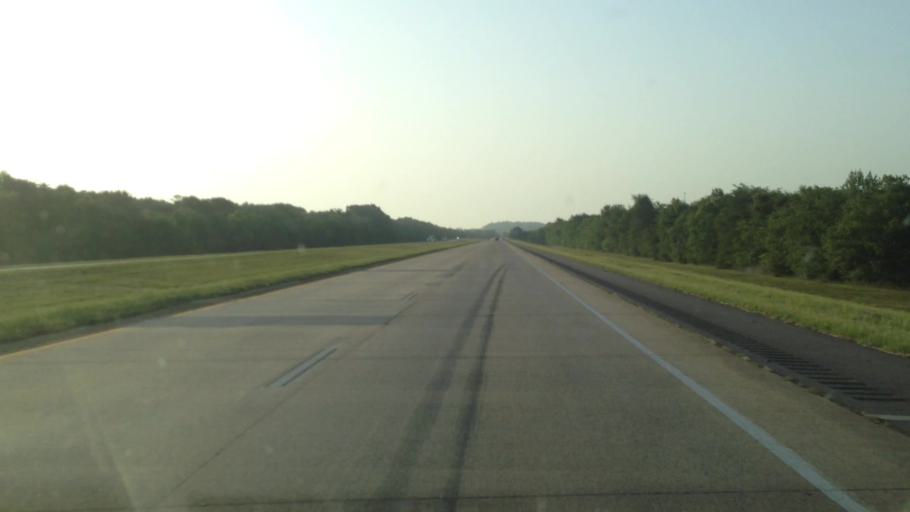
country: US
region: Louisiana
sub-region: Grant Parish
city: Colfax
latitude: 31.5052
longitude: -92.8824
